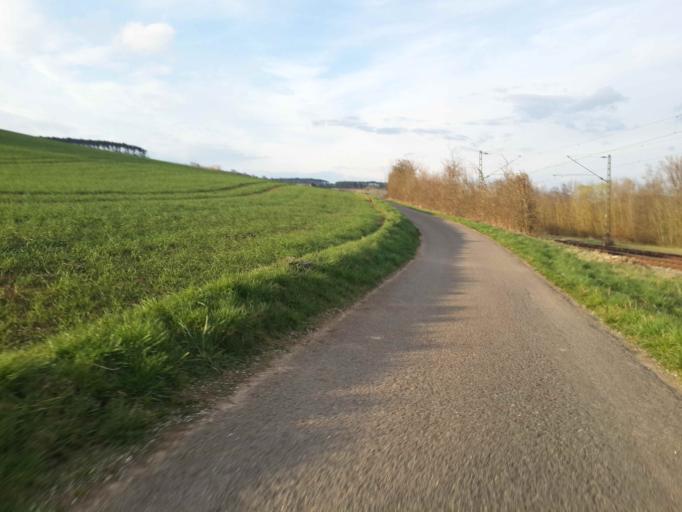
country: DE
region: Baden-Wuerttemberg
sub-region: Regierungsbezirk Stuttgart
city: Boxberg
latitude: 49.5036
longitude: 9.6783
